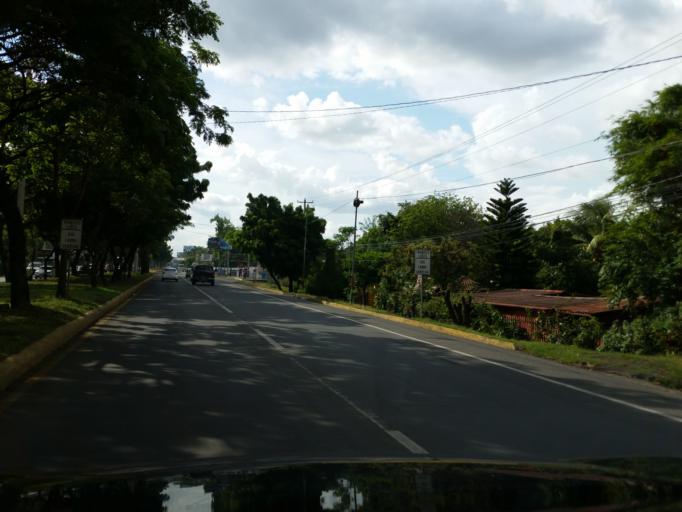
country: NI
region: Masaya
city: Ticuantepe
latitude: 12.0623
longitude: -86.2089
